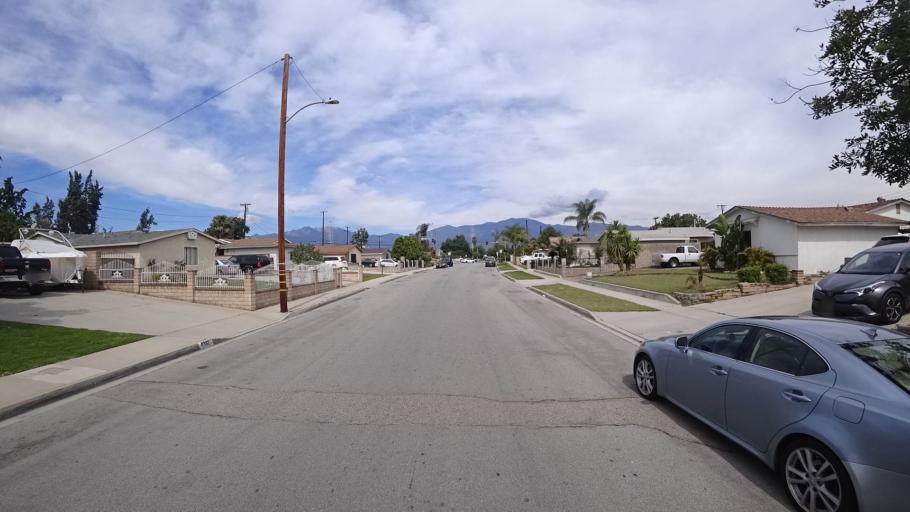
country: US
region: California
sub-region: Los Angeles County
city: Baldwin Park
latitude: 34.0910
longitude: -117.9818
